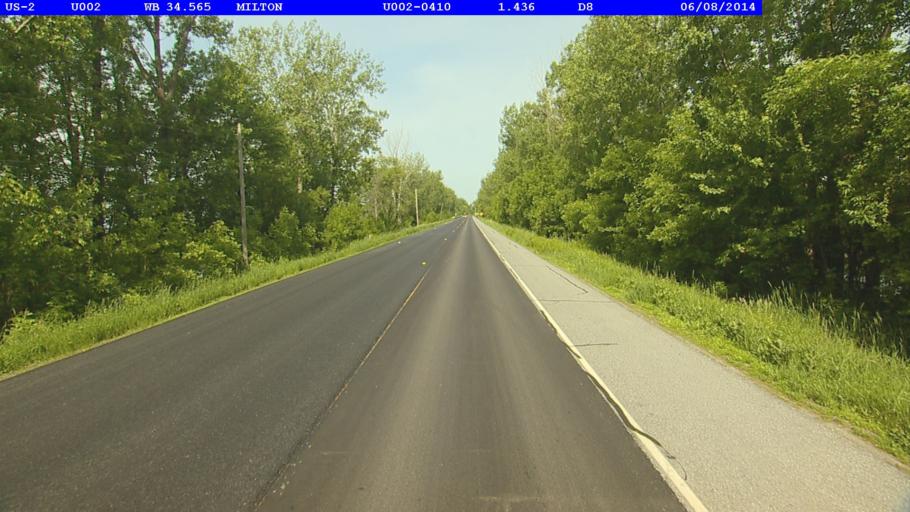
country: US
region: Vermont
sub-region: Chittenden County
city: Colchester
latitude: 44.6246
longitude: -73.2290
